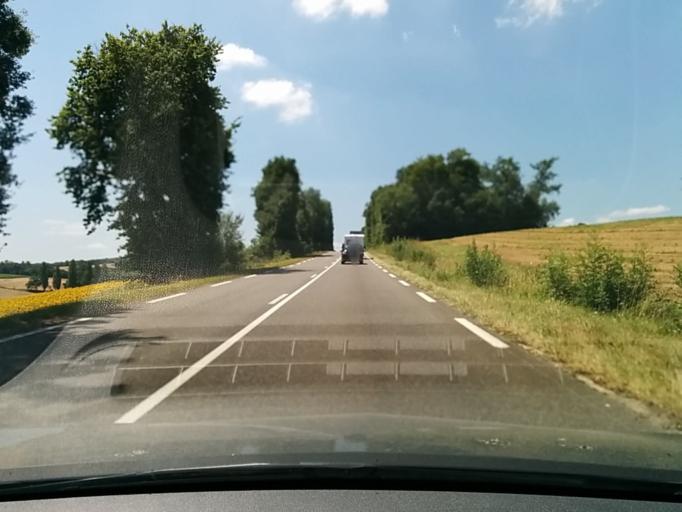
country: FR
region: Midi-Pyrenees
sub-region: Departement du Gers
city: Vic-Fezensac
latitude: 43.7578
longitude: 0.2221
